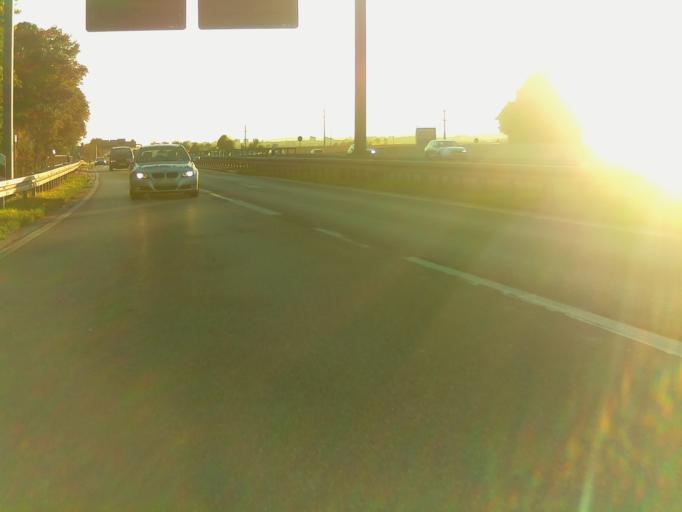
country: DE
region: Hesse
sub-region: Regierungsbezirk Darmstadt
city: Bad Homburg vor der Hoehe
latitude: 50.2012
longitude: 8.6463
